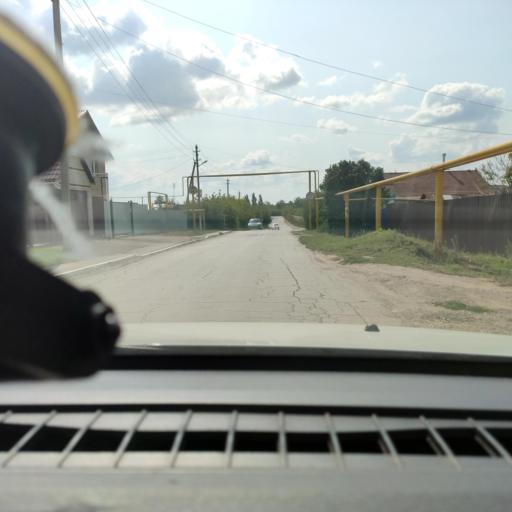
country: RU
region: Samara
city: Chapayevsk
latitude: 53.0096
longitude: 49.7436
